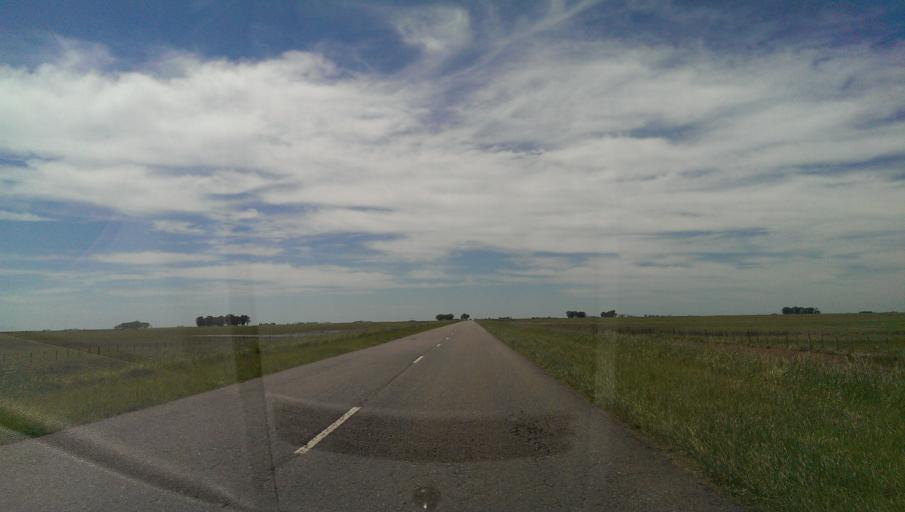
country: AR
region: Buenos Aires
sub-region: Partido de General La Madrid
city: General La Madrid
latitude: -37.4339
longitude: -61.0834
